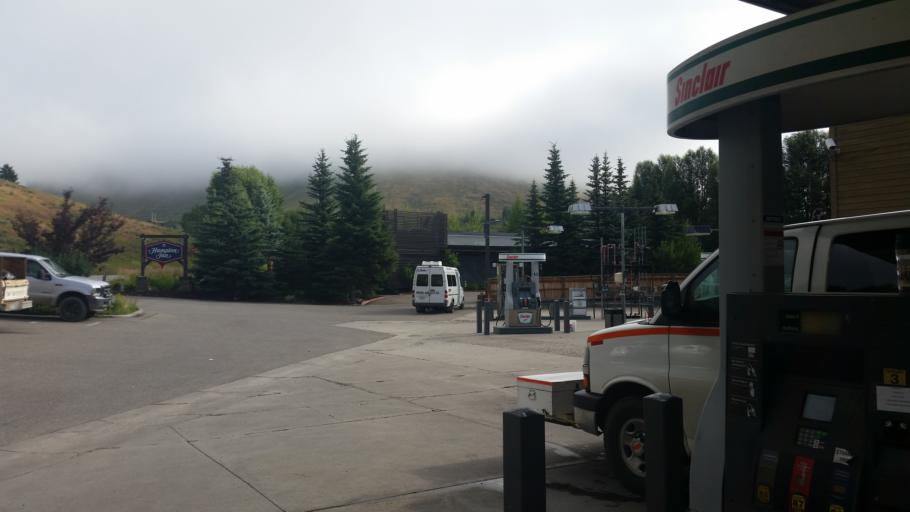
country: US
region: Wyoming
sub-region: Teton County
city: Jackson
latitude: 43.4705
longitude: -110.7910
